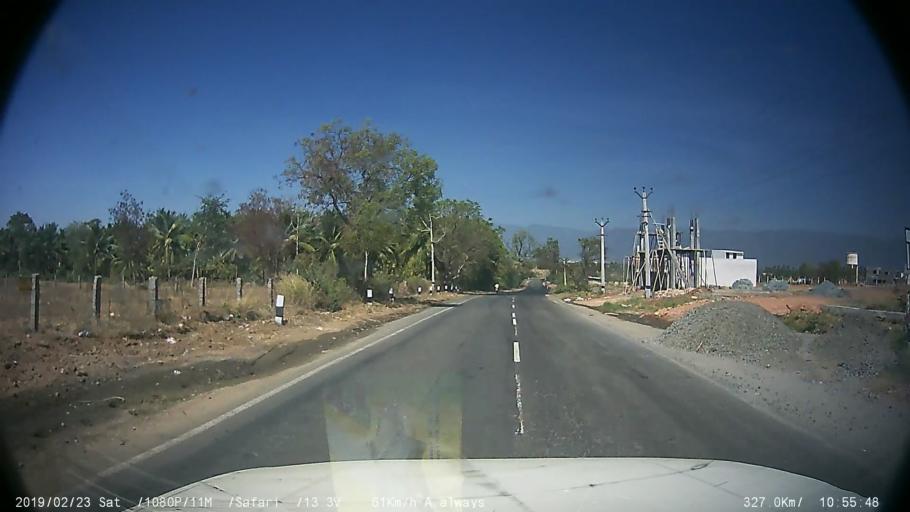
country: IN
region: Tamil Nadu
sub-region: Coimbatore
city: Sirumugai
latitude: 11.2590
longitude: 77.0350
